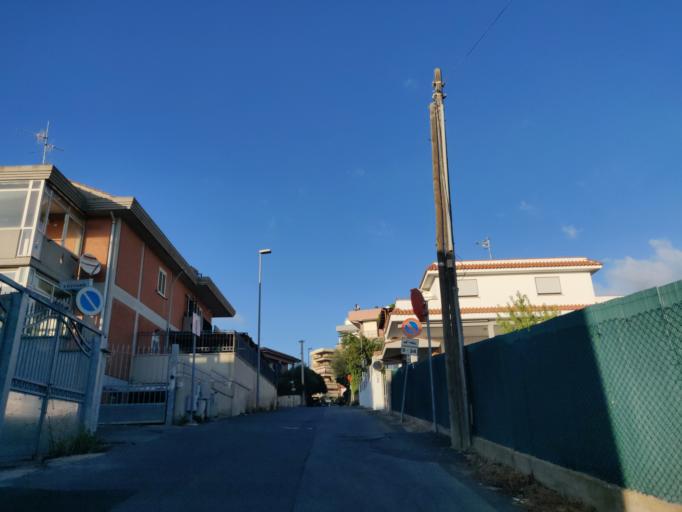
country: IT
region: Latium
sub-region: Citta metropolitana di Roma Capitale
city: Civitavecchia
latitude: 42.0927
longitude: 11.8119
